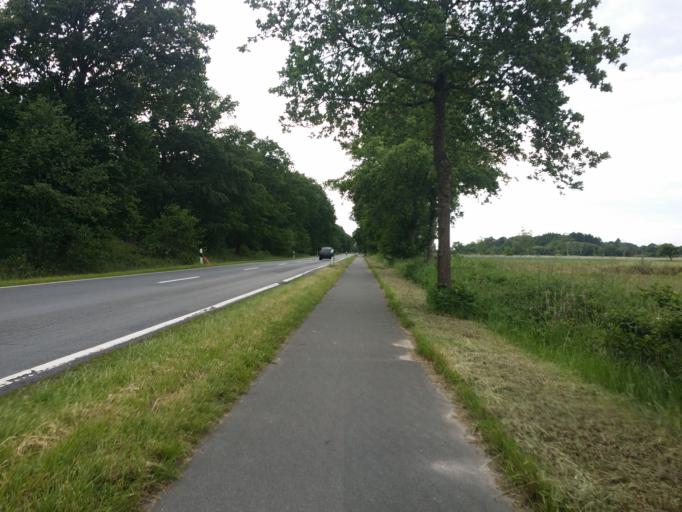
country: DE
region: Lower Saxony
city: Friedeburg
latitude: 53.5059
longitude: 7.8083
